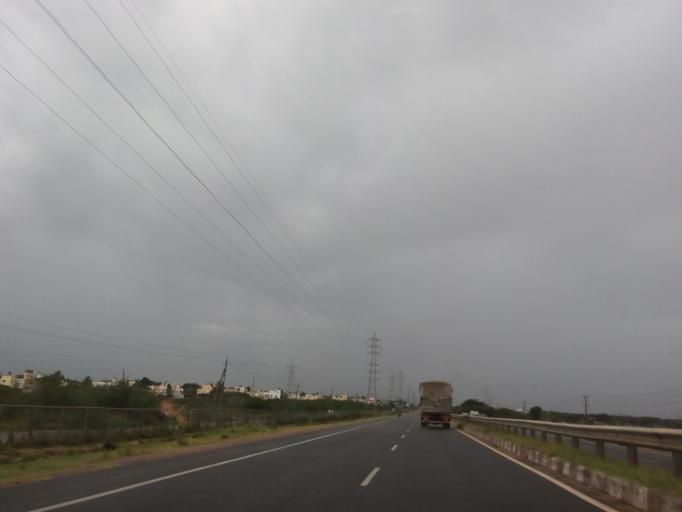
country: IN
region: Karnataka
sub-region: Davanagere
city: Harihar
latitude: 14.4381
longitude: 75.9066
